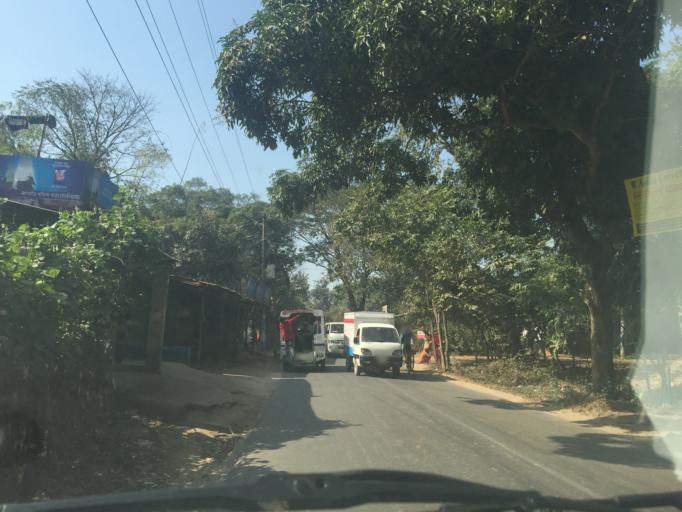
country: BD
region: Dhaka
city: Tungi
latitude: 23.8577
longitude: 90.3150
